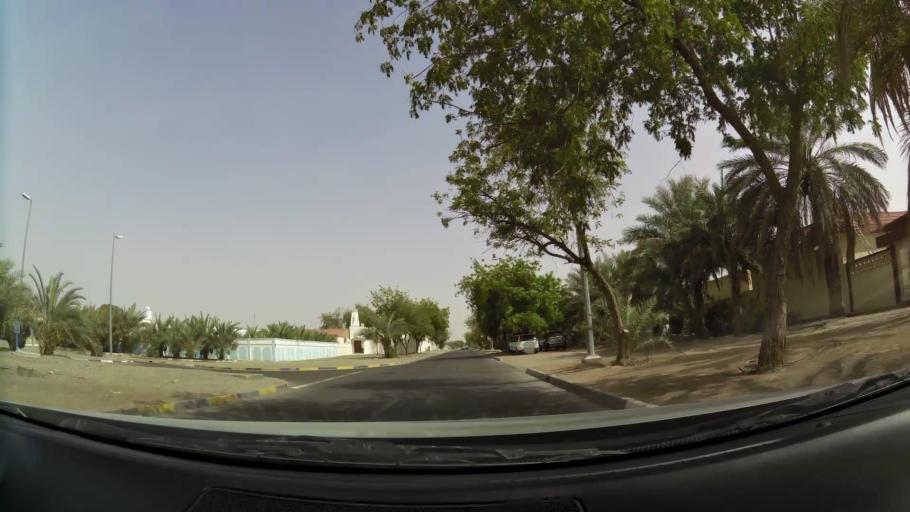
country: AE
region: Abu Dhabi
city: Al Ain
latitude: 24.1949
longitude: 55.6346
